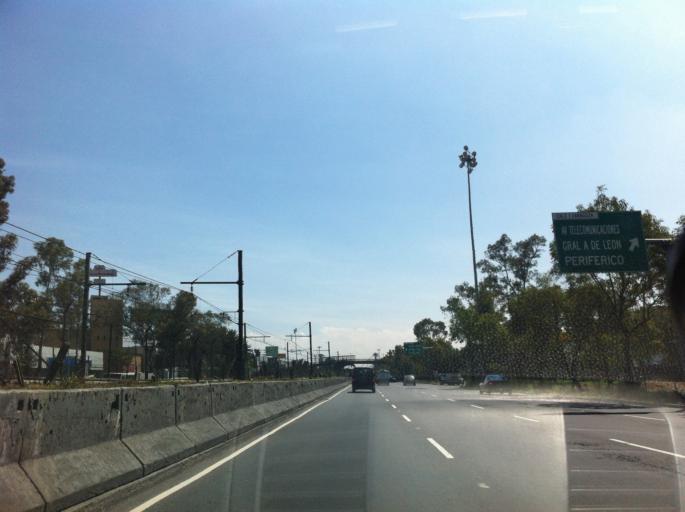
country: MX
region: Mexico City
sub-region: Iztacalco
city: Iztacalco
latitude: 19.4009
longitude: -99.0634
